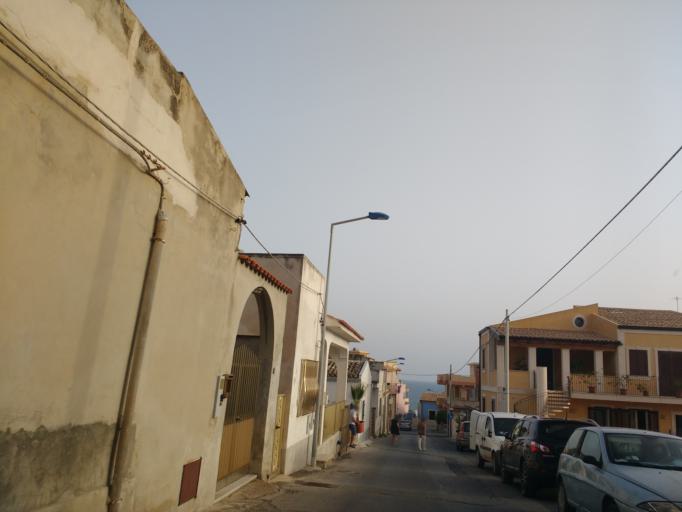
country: IT
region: Sicily
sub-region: Ragusa
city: Cava d'Aliga
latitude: 36.7313
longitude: 14.6833
